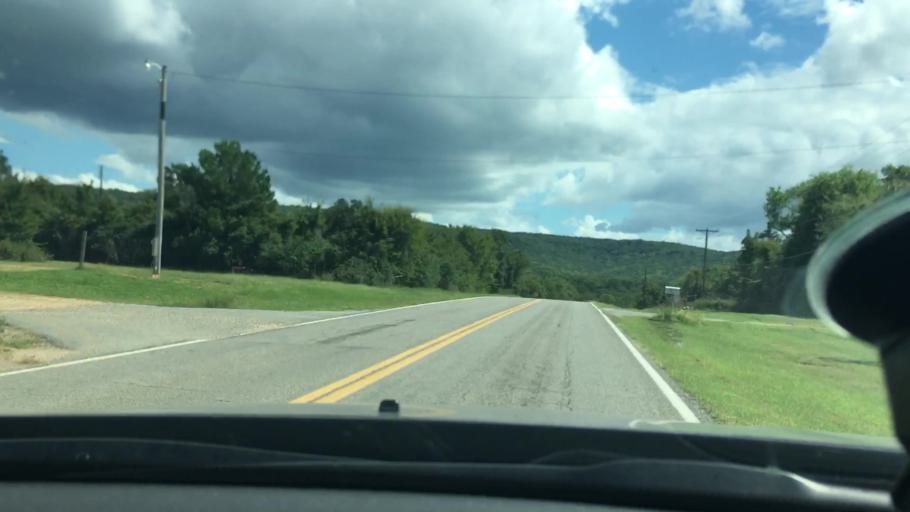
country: US
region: Oklahoma
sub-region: Cherokee County
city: Park Hill
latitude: 35.6909
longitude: -94.9121
